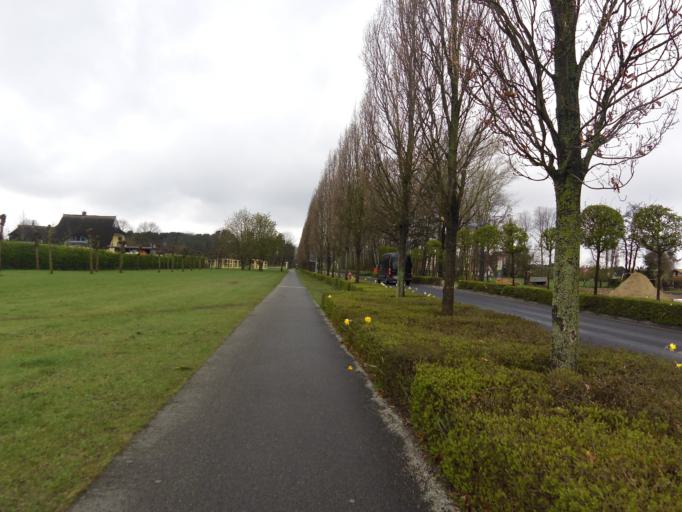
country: DE
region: Mecklenburg-Vorpommern
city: Zingst
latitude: 54.4345
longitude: 12.7016
